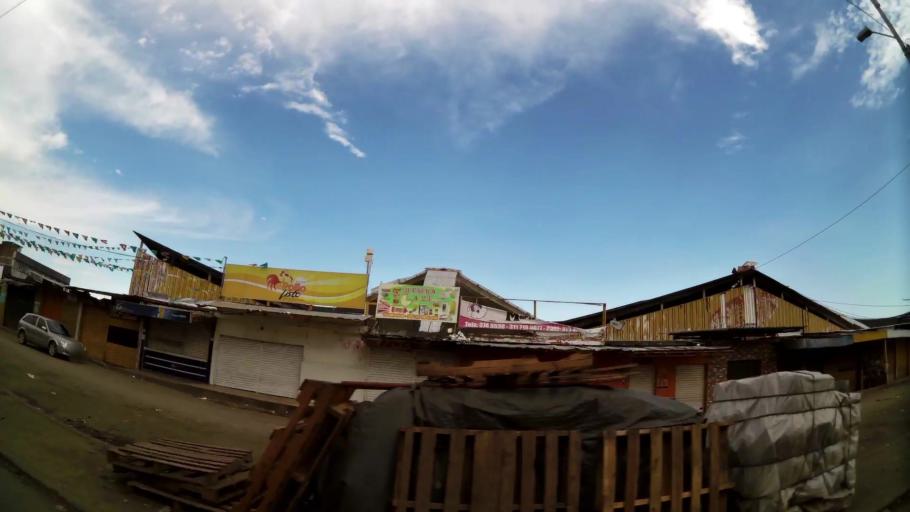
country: CO
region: Valle del Cauca
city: Cali
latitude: 3.4277
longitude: -76.5210
